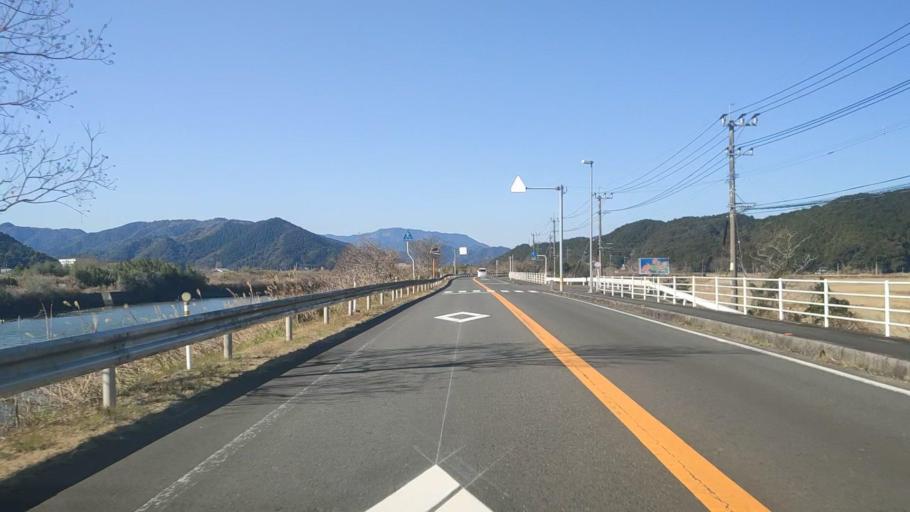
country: JP
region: Oita
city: Saiki
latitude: 32.9357
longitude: 131.9195
